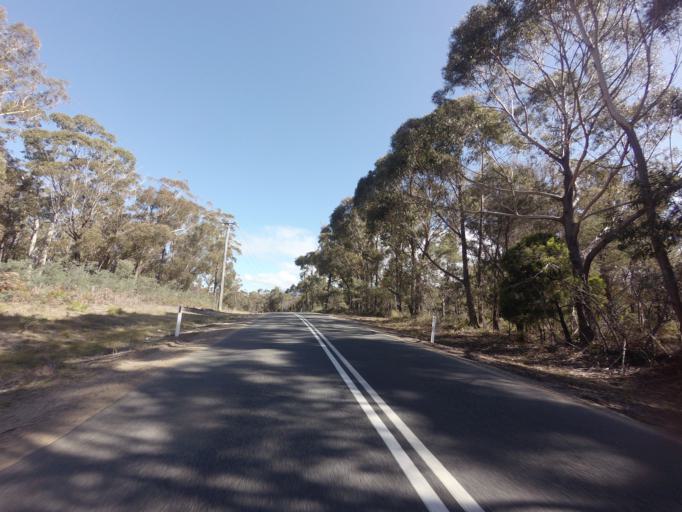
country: AU
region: Tasmania
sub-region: Break O'Day
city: St Helens
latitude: -41.6884
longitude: 148.2801
